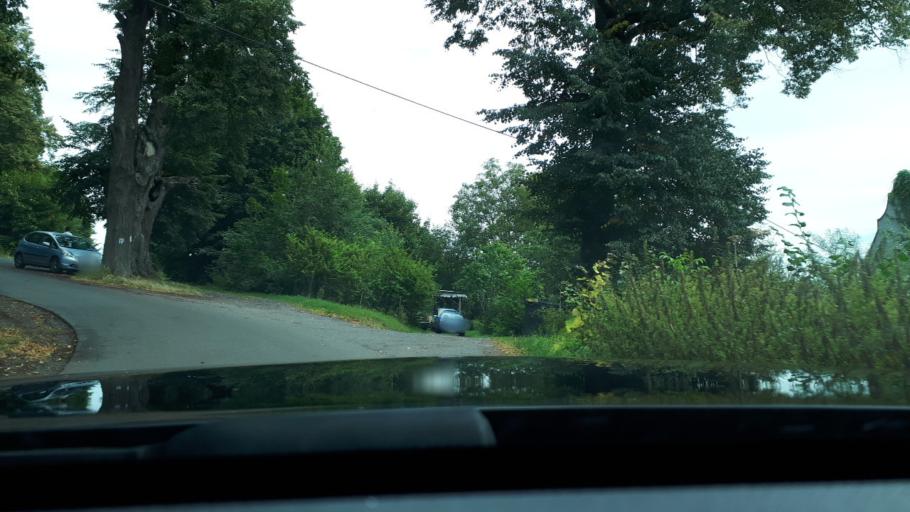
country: PL
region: Lower Silesian Voivodeship
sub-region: Powiat zlotoryjski
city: Olszanica
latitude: 51.1742
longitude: 15.7626
